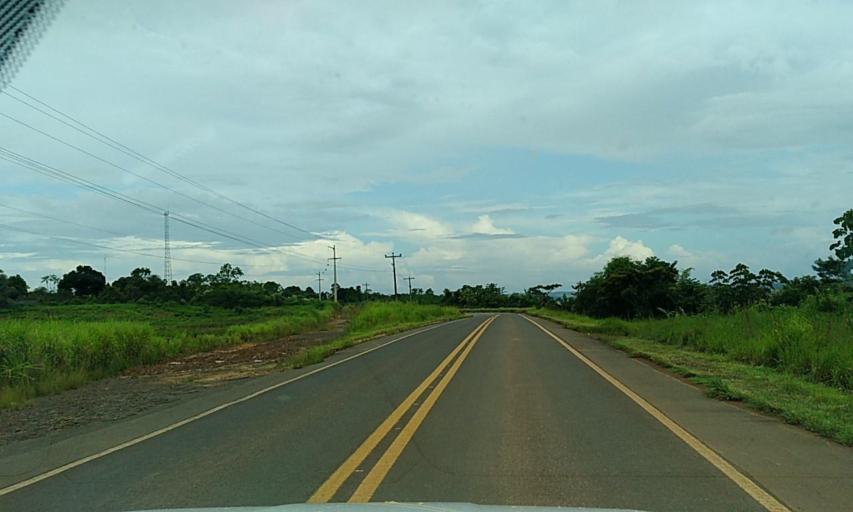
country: BR
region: Para
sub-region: Altamira
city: Altamira
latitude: -3.3615
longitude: -52.6354
